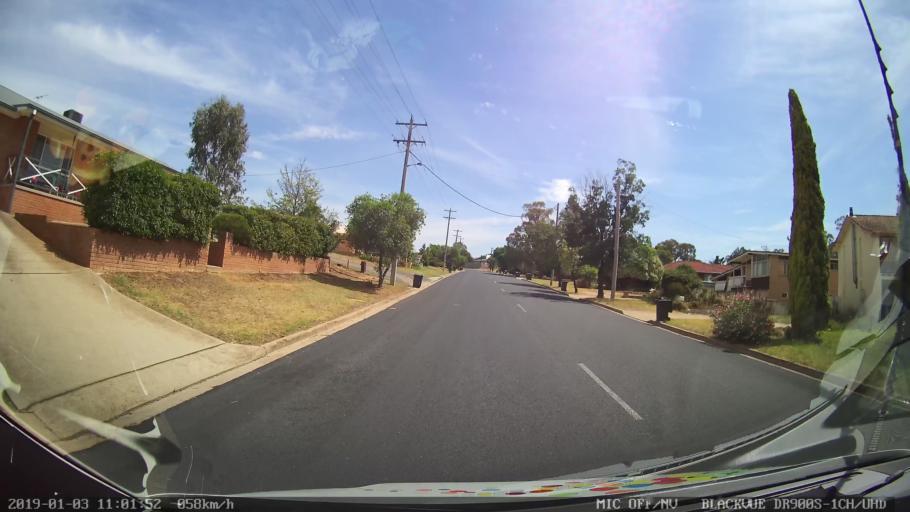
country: AU
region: New South Wales
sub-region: Young
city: Young
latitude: -34.3020
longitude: 148.2992
